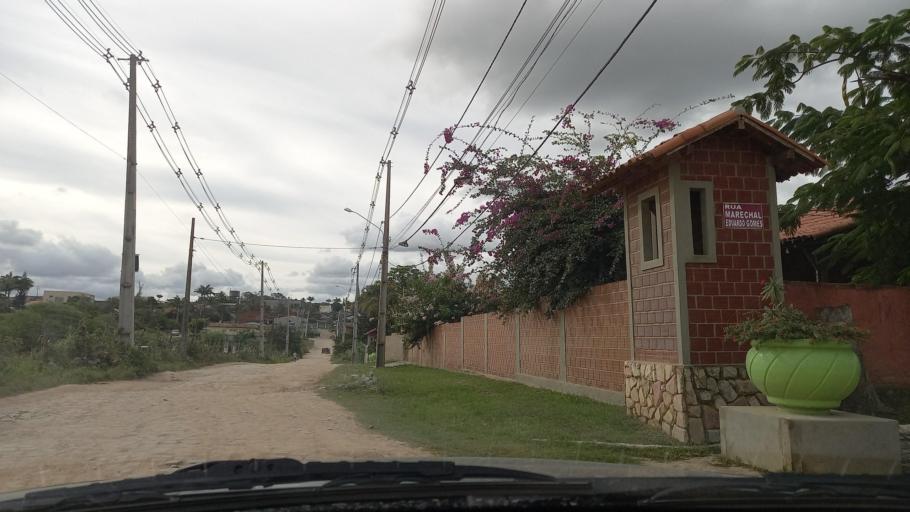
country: BR
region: Pernambuco
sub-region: Gravata
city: Gravata
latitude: -8.1985
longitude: -35.5496
